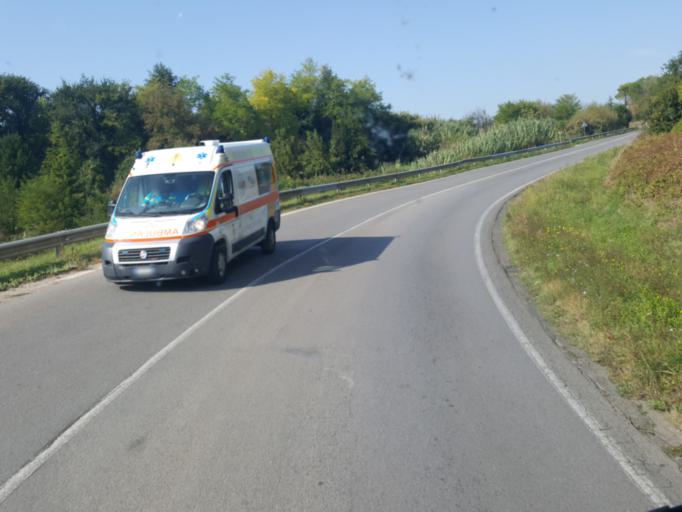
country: IT
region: Tuscany
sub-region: Provincia di Siena
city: Colle di Val d'Elsa
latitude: 43.4128
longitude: 11.1063
